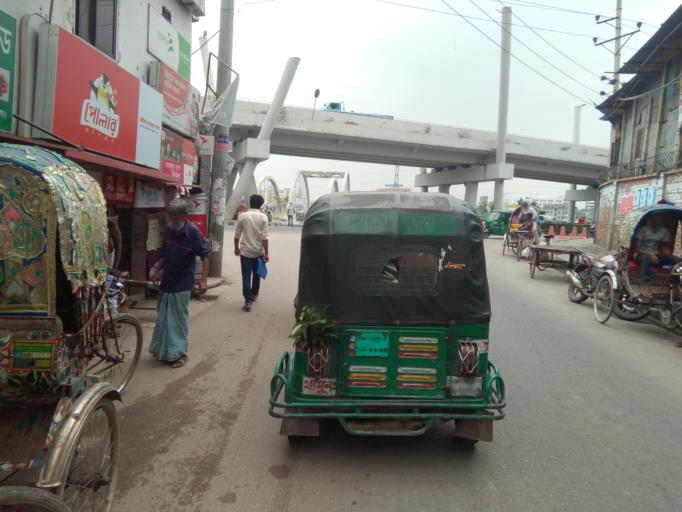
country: BD
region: Dhaka
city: Paltan
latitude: 23.7602
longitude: 90.4108
